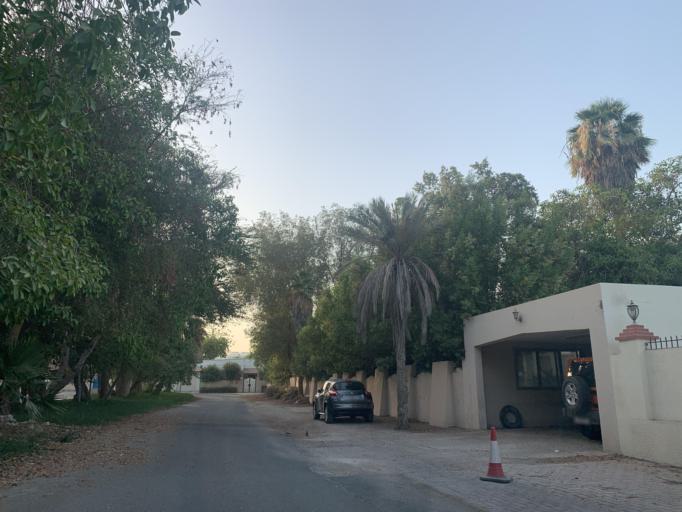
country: BH
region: Manama
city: Jidd Hafs
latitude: 26.2212
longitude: 50.5304
